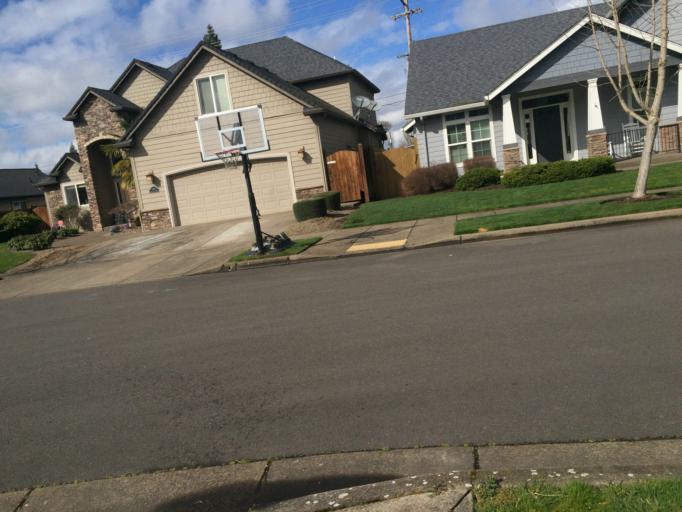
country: US
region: Oregon
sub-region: Lane County
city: Eugene
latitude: 44.1027
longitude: -123.1548
